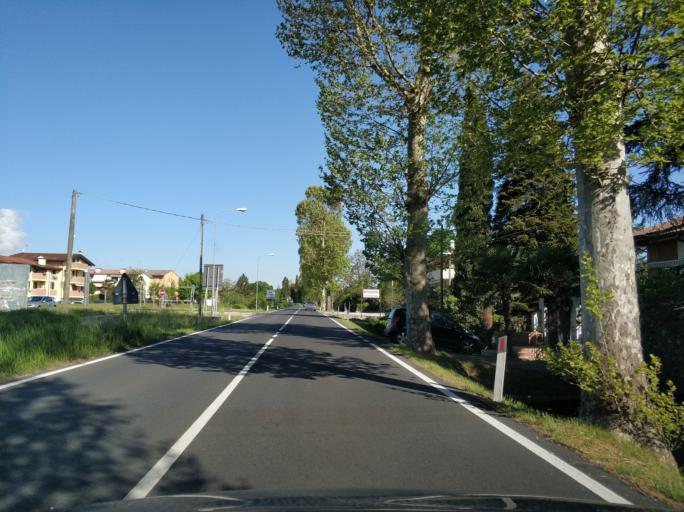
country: IT
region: Friuli Venezia Giulia
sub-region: Provincia di Udine
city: Terzo d'Aquileia
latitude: 45.8015
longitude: 13.3482
